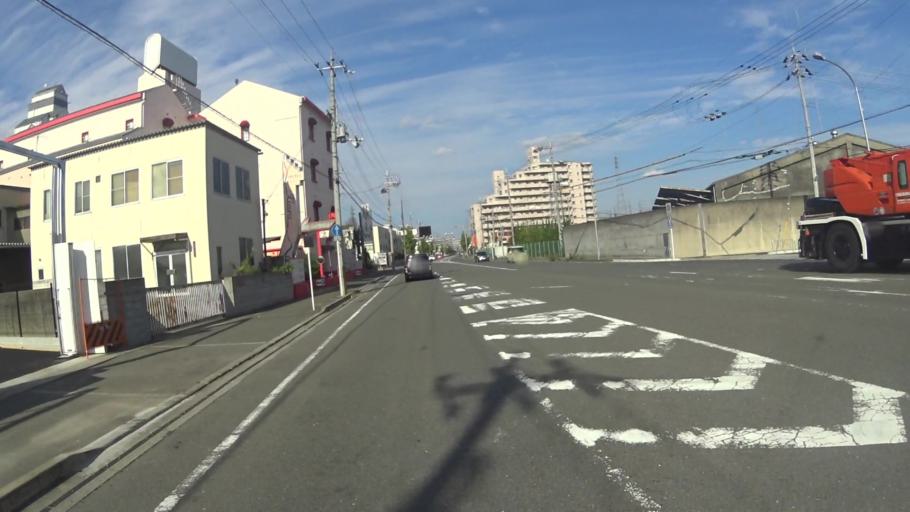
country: JP
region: Kyoto
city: Yawata
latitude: 34.8970
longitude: 135.7041
